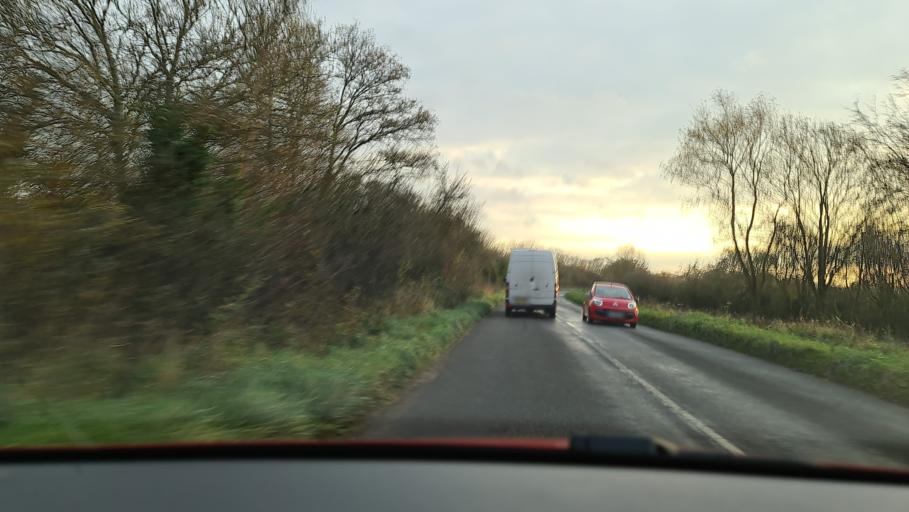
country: GB
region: England
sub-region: Oxfordshire
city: Kidlington
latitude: 51.8520
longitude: -1.2647
